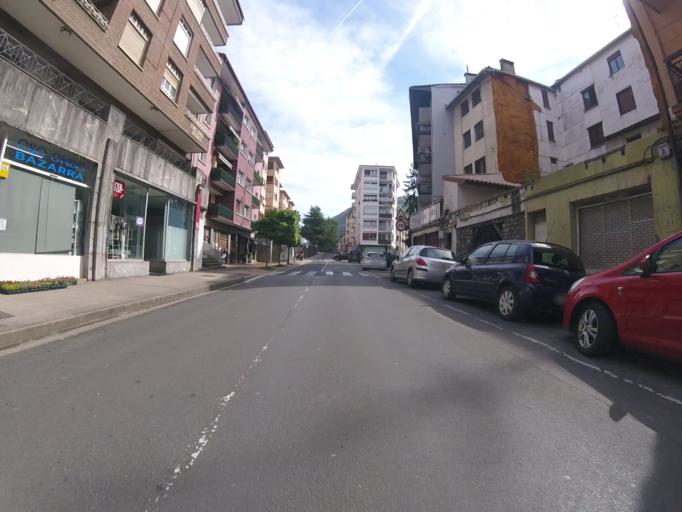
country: ES
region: Basque Country
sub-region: Provincia de Guipuzcoa
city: Azpeitia
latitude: 43.1818
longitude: -2.2691
